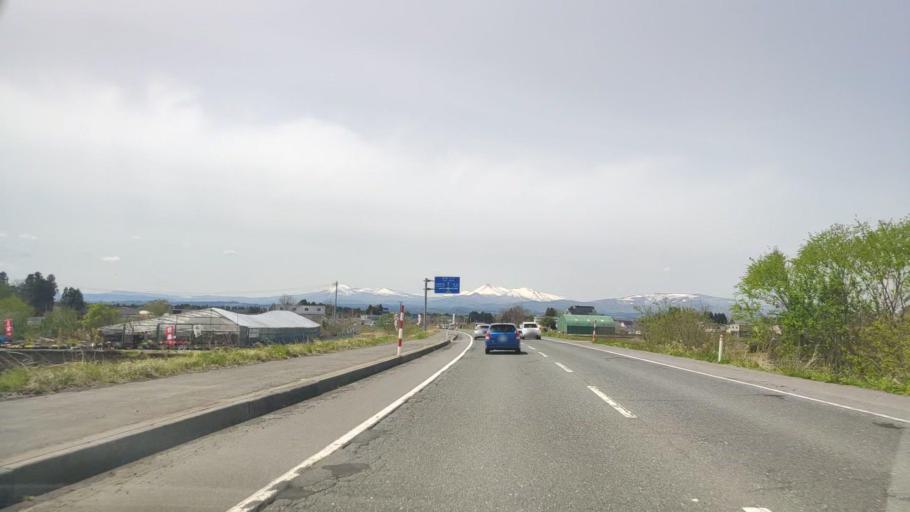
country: JP
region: Aomori
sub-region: Misawa Shi
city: Inuotose
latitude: 40.6391
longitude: 141.2350
